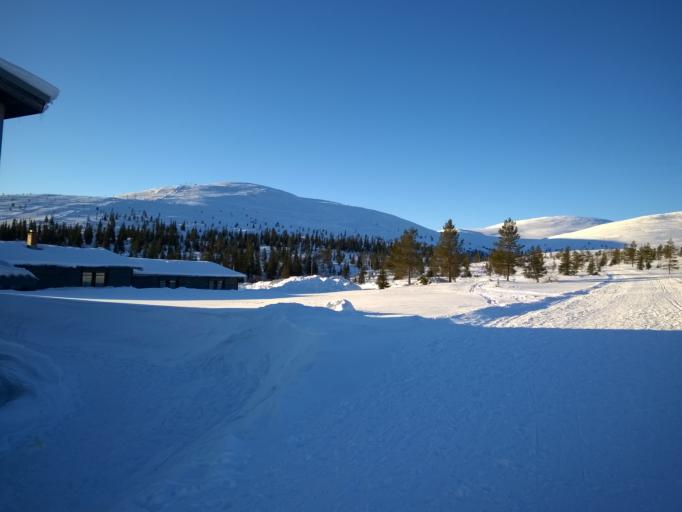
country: FI
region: Lapland
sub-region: Tunturi-Lappi
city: Muonio
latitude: 68.0465
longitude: 24.0635
